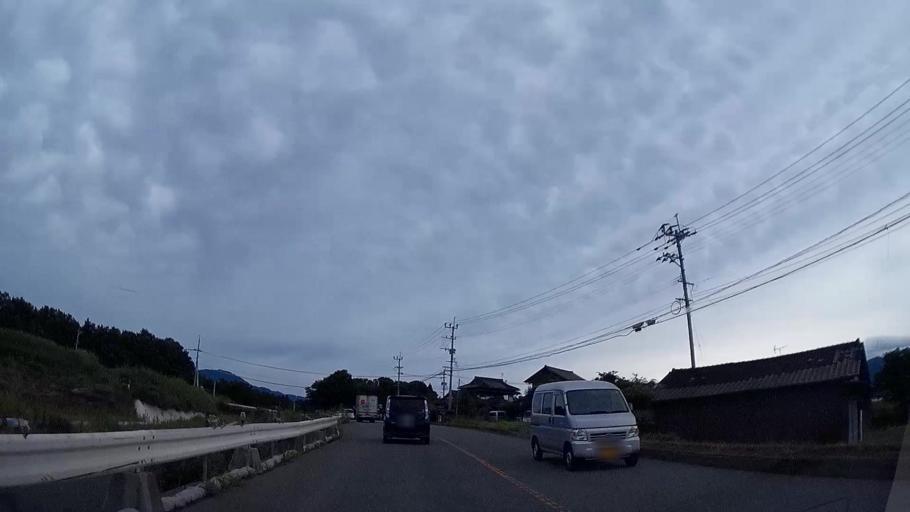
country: JP
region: Kumamoto
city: Kikuchi
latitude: 32.9485
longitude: 130.8236
